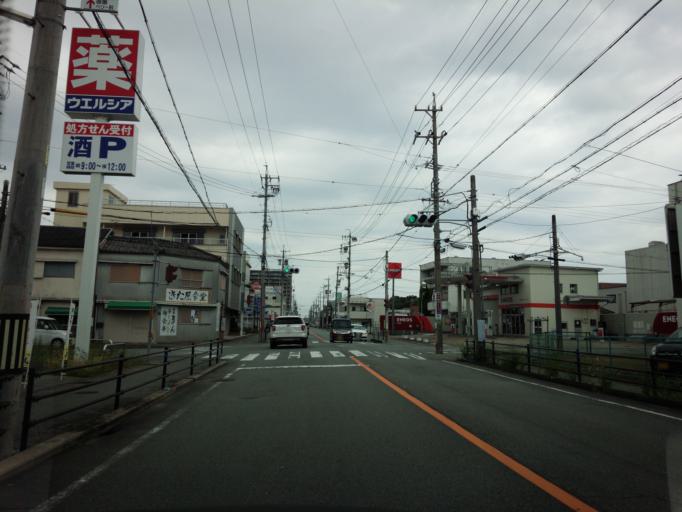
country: JP
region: Mie
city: Ise
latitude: 34.4931
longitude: 136.7131
